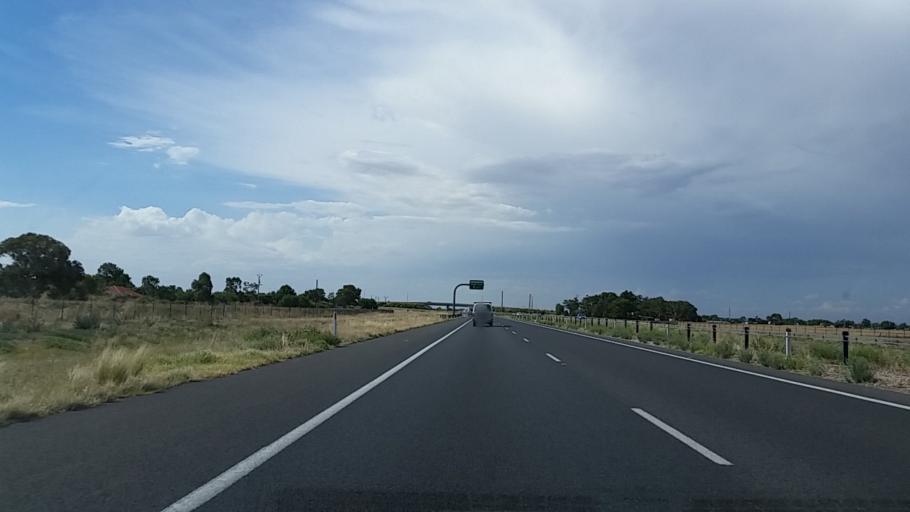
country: AU
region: South Australia
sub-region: Playford
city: Angle Vale
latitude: -34.6425
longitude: 138.6675
